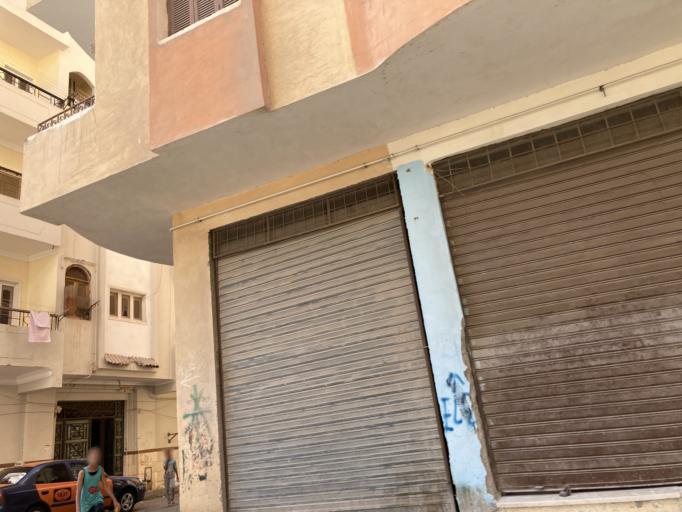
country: EG
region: Red Sea
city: Hurghada
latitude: 27.2490
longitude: 33.8332
